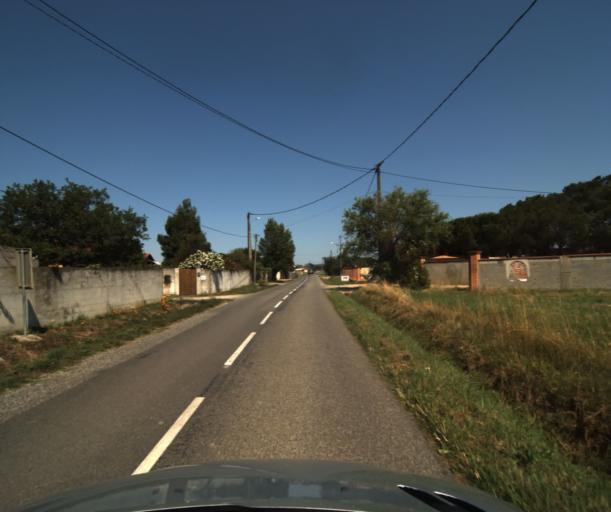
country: FR
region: Midi-Pyrenees
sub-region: Departement de la Haute-Garonne
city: Saubens
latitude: 43.4774
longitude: 1.3613
